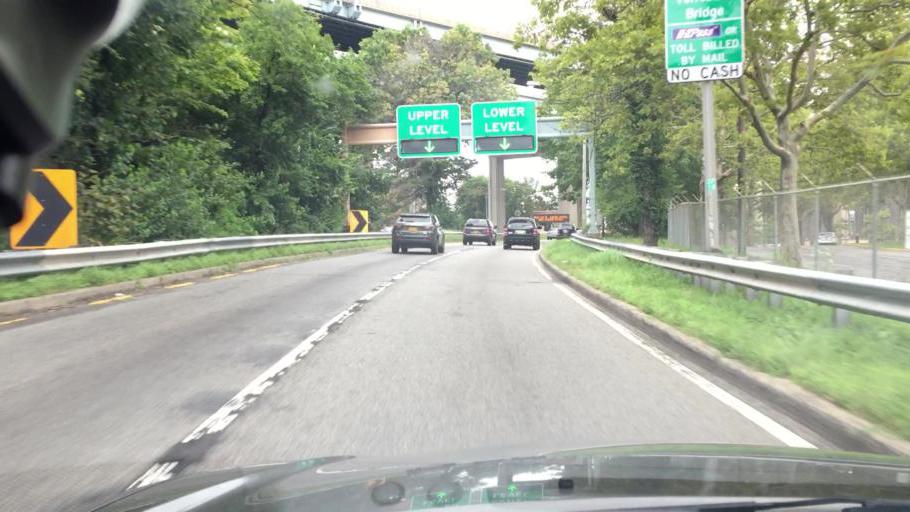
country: US
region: New York
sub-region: Kings County
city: Bensonhurst
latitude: 40.6091
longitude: -74.0331
